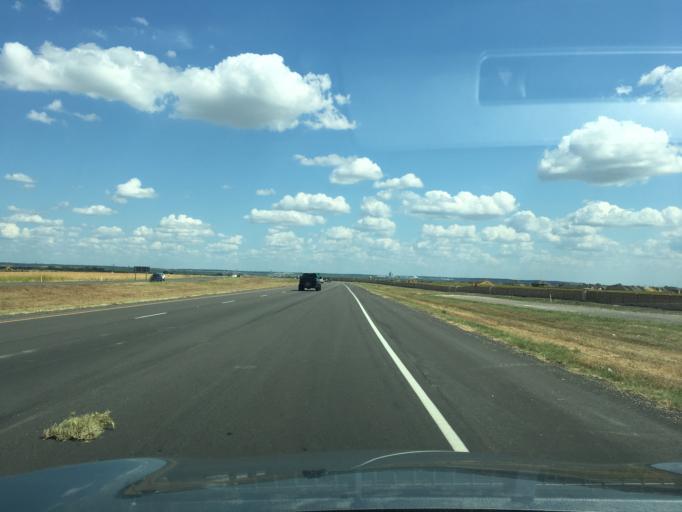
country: US
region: Texas
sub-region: Tarrant County
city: Mansfield
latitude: 32.5322
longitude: -97.0995
